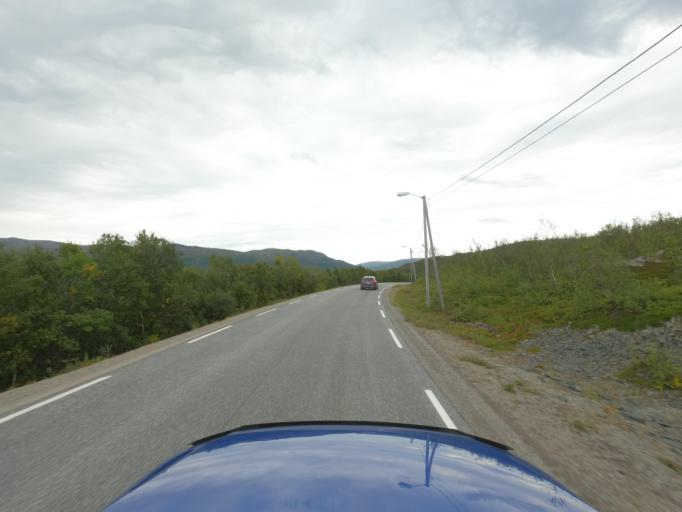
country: NO
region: Finnmark Fylke
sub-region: Kvalsund
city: Kvalsund
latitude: 70.4773
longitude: 24.2495
